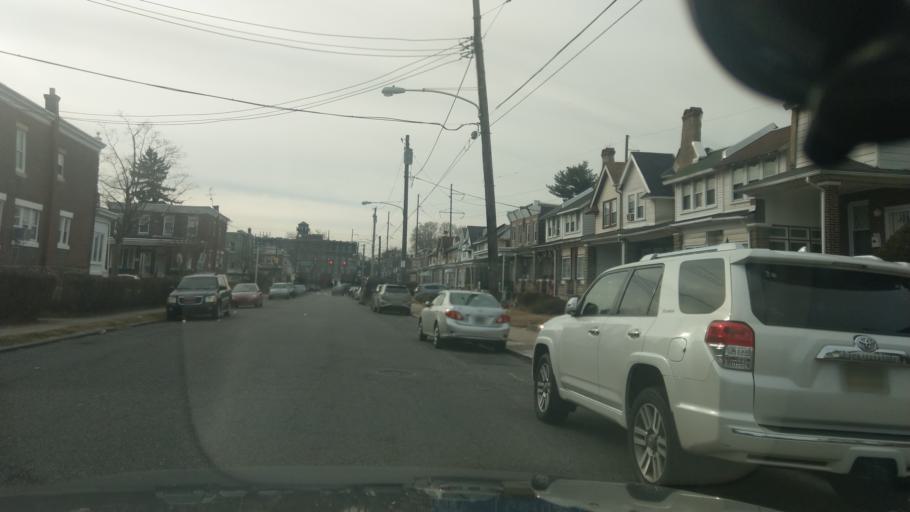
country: US
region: Pennsylvania
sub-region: Montgomery County
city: Wyncote
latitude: 40.0382
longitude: -75.1339
